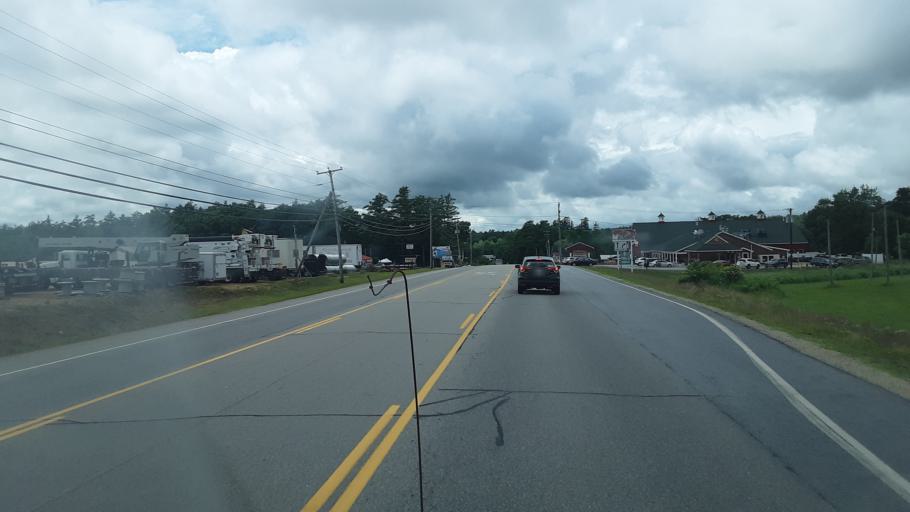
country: US
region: New Hampshire
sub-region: Merrimack County
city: Epsom
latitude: 43.2227
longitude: -71.2479
